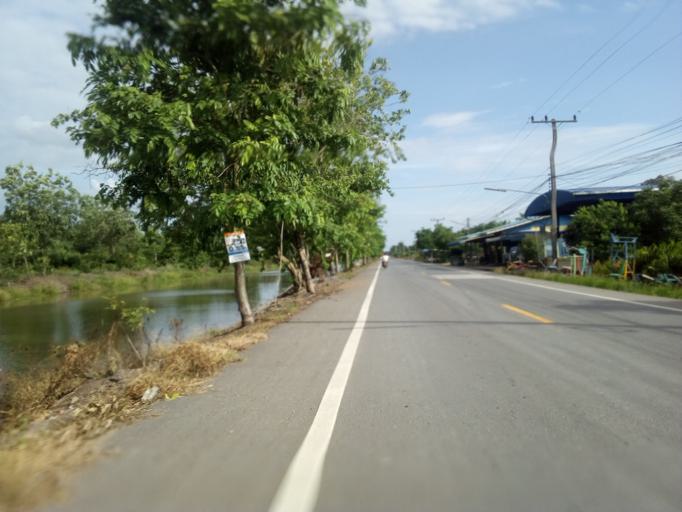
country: TH
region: Pathum Thani
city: Nong Suea
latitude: 14.1642
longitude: 100.8459
